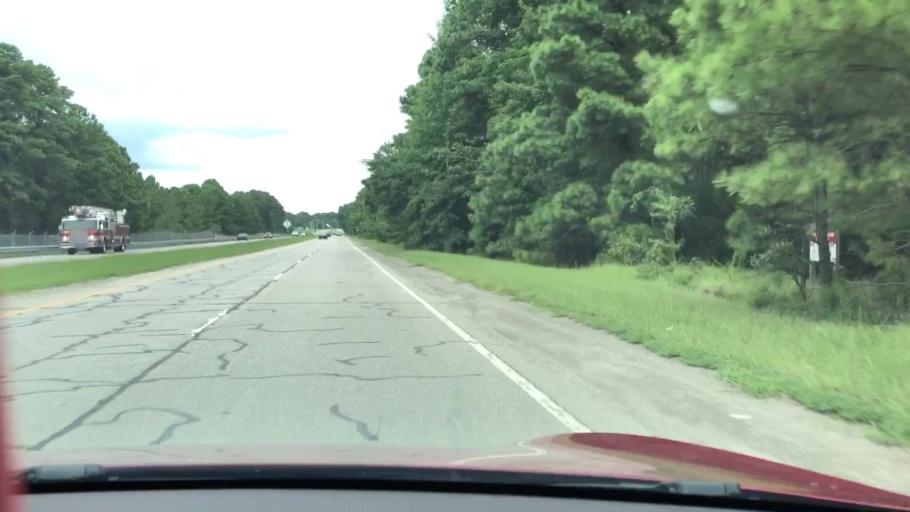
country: US
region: Virginia
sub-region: City of Virginia Beach
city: Virginia Beach
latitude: 36.8291
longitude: -76.0106
